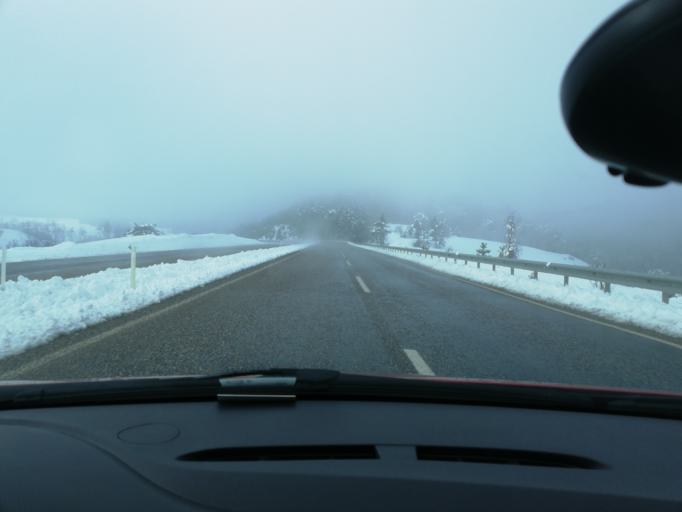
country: TR
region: Kastamonu
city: Akkaya
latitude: 41.2928
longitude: 33.4773
